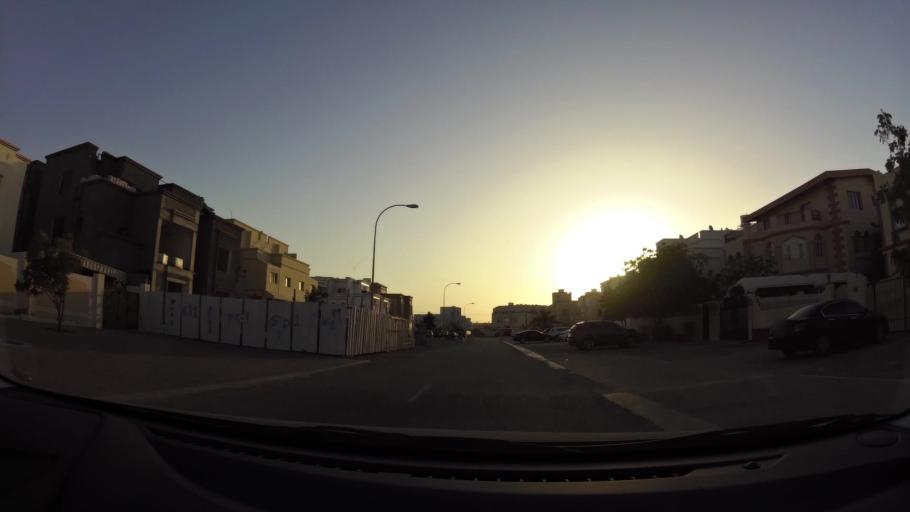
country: OM
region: Muhafazat Masqat
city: As Sib al Jadidah
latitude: 23.6135
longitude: 58.2002
